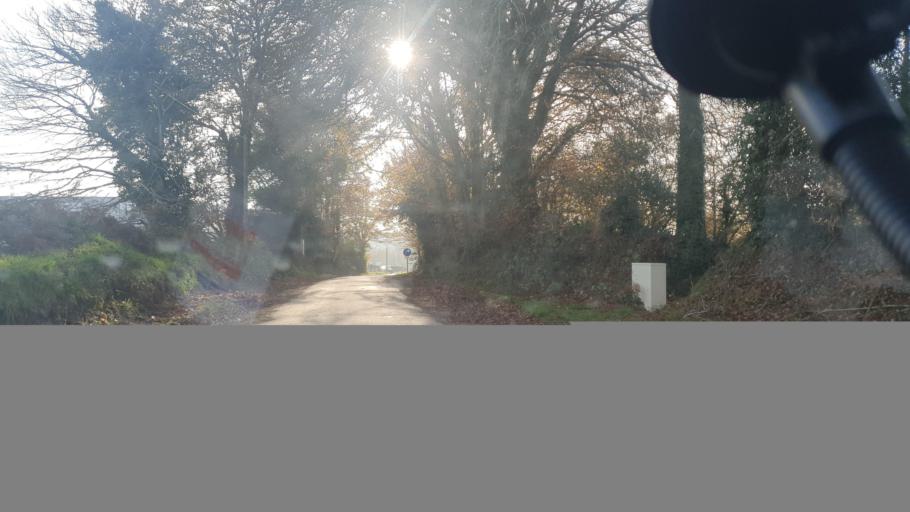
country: FR
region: Brittany
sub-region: Departement du Finistere
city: Briec
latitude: 48.1058
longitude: -4.0239
